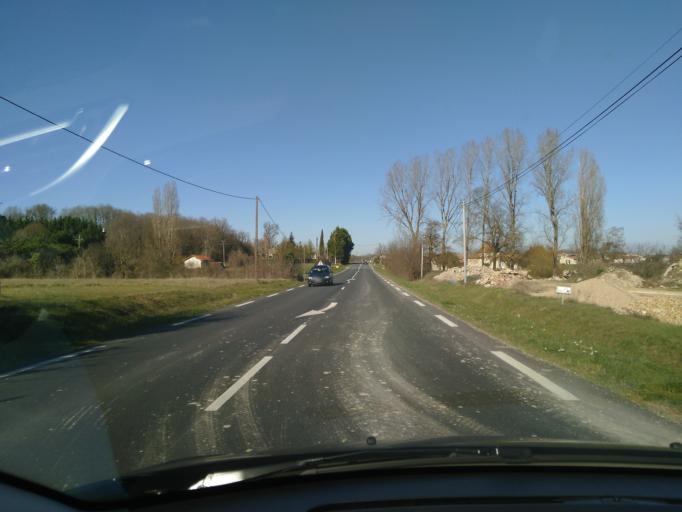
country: FR
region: Aquitaine
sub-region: Departement de la Dordogne
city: Monbazillac
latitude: 44.7461
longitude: 0.5375
